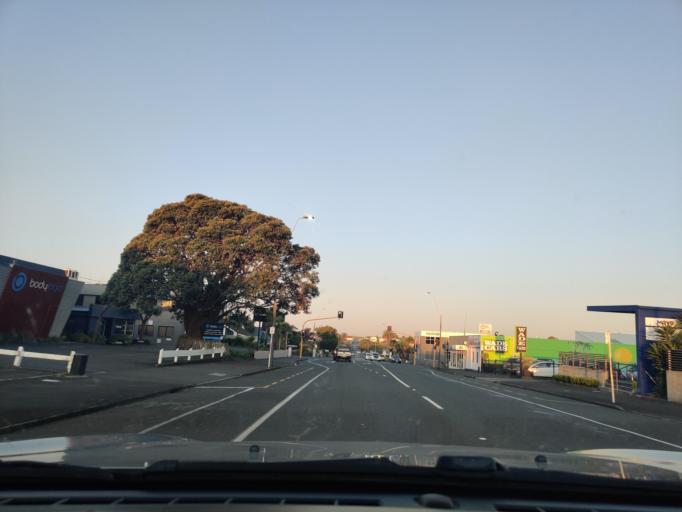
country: NZ
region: Taranaki
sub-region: New Plymouth District
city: New Plymouth
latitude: -39.0543
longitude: 174.0856
